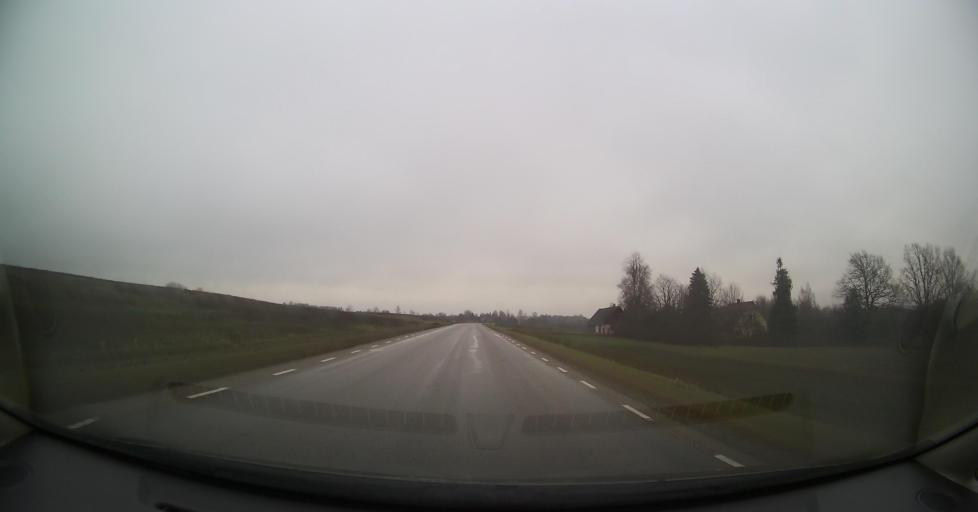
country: EE
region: Tartu
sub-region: Tartu linn
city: Tartu
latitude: 58.3839
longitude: 26.9781
